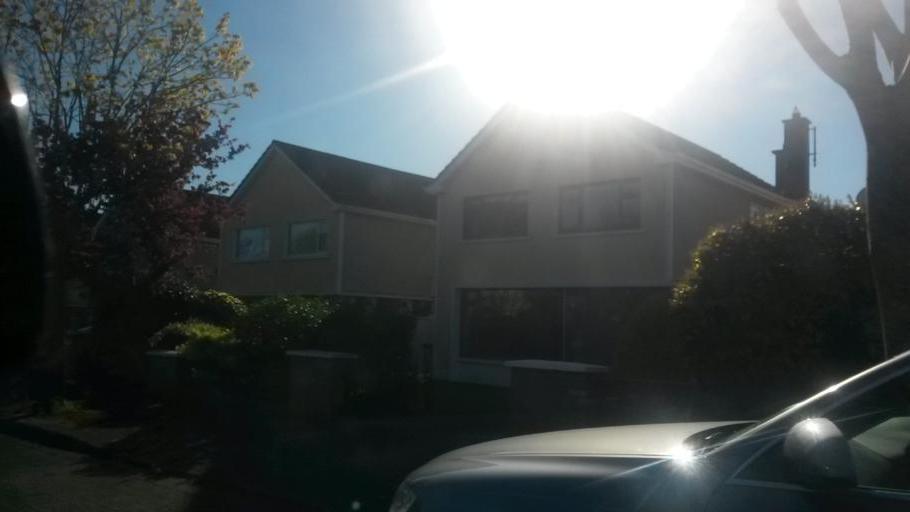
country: IE
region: Leinster
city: Sutton
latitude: 53.3765
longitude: -6.0980
